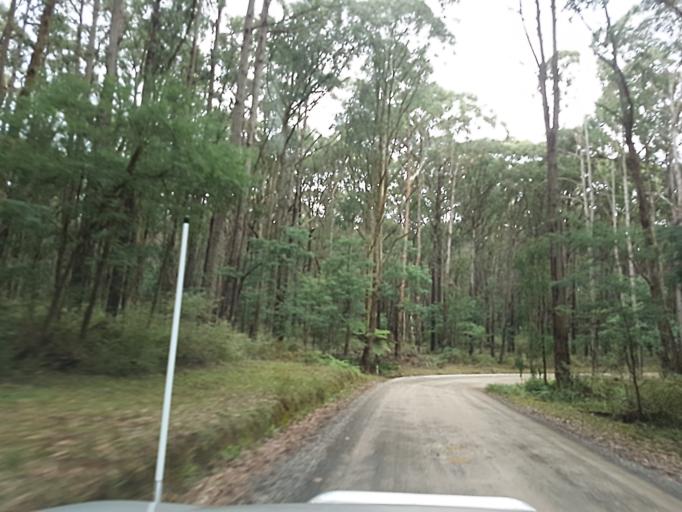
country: AU
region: Victoria
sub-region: Yarra Ranges
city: Mount Dandenong
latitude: -37.8361
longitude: 145.3976
